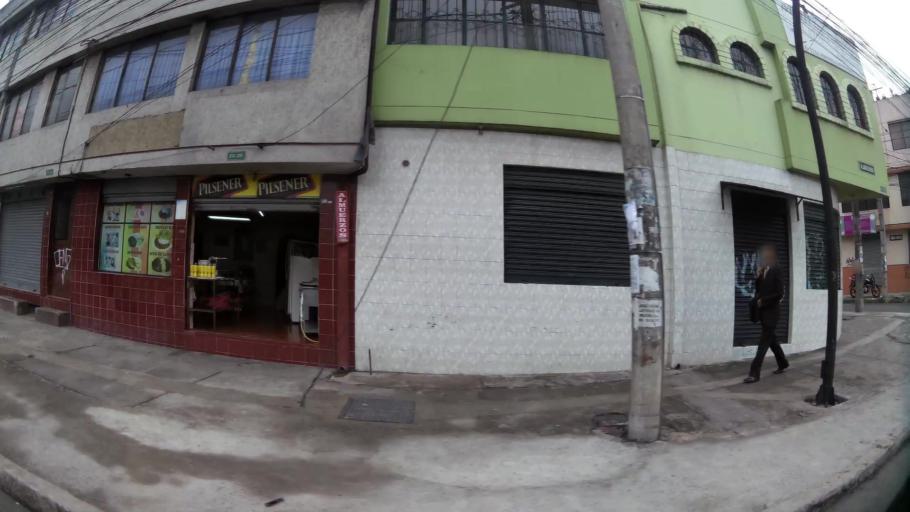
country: EC
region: Pichincha
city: Quito
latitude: -0.2124
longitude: -78.4847
